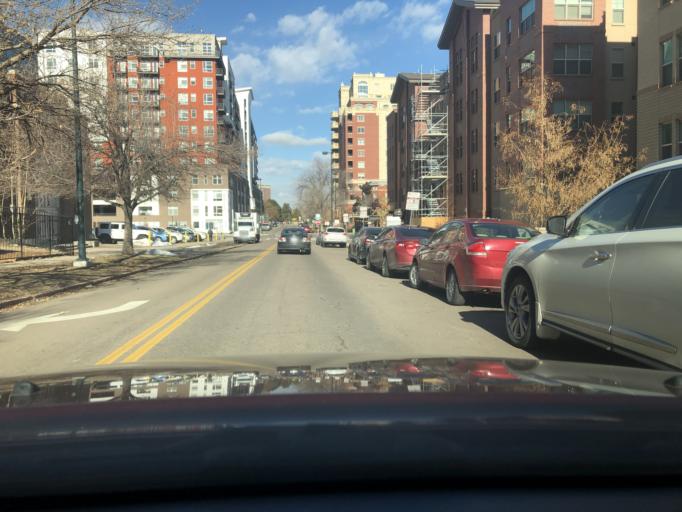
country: US
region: Colorado
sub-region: Denver County
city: Denver
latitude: 39.7452
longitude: -104.9823
